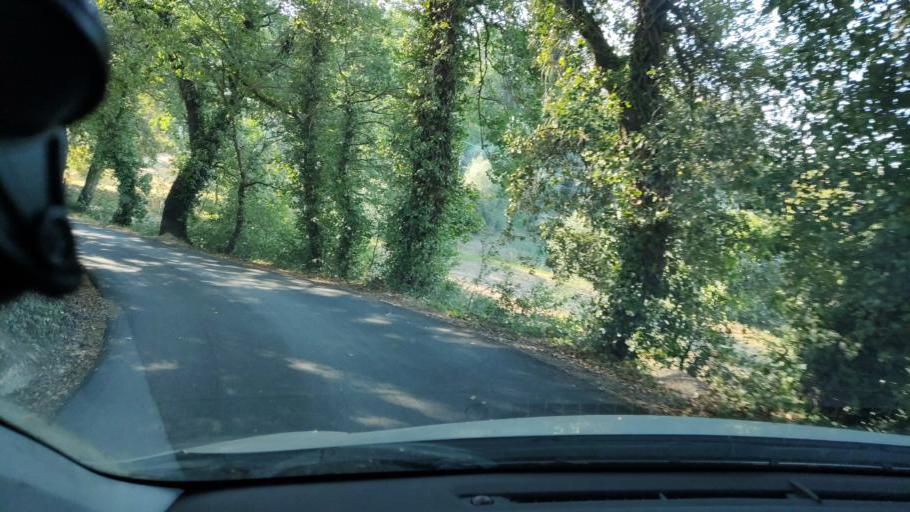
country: IT
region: Umbria
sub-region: Provincia di Terni
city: Amelia
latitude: 42.5439
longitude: 12.3995
